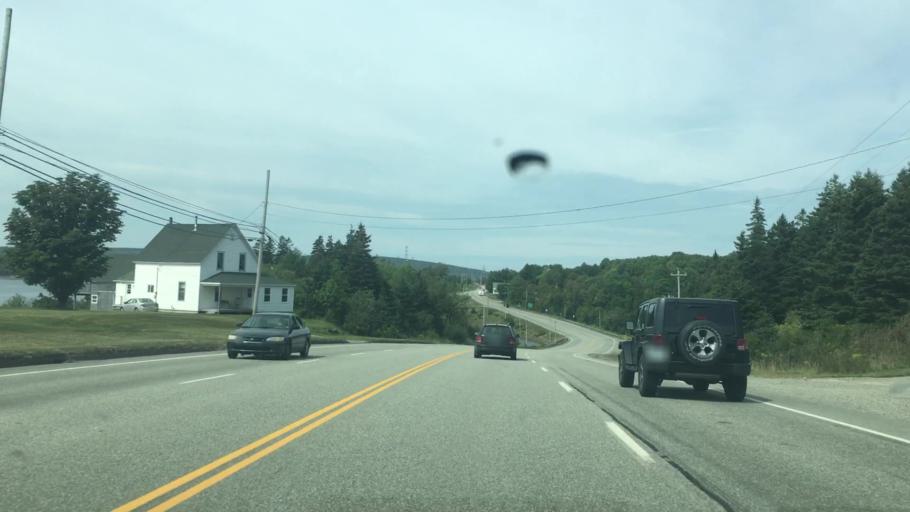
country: CA
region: Nova Scotia
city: Port Hawkesbury
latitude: 45.6432
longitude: -61.3936
